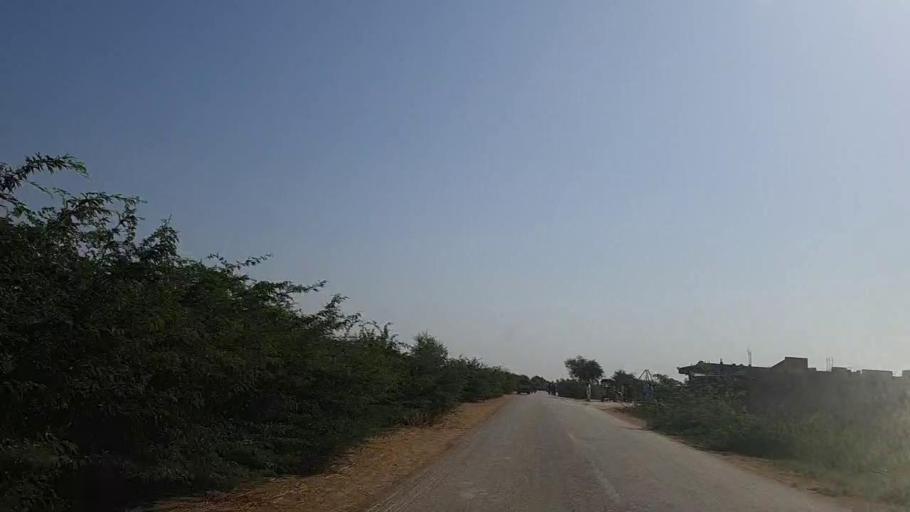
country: PK
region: Sindh
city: Mirpur Batoro
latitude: 24.6093
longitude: 68.2961
